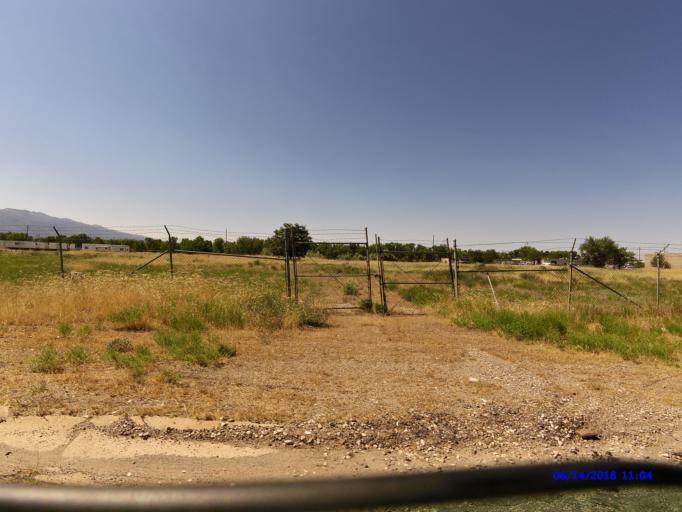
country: US
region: Utah
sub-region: Weber County
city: Ogden
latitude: 41.2133
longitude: -112.0032
